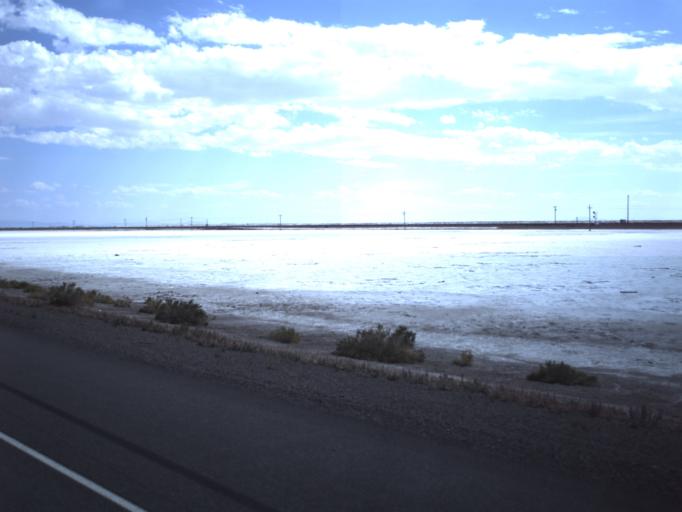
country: US
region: Utah
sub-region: Tooele County
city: Wendover
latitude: 40.7384
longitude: -113.8491
